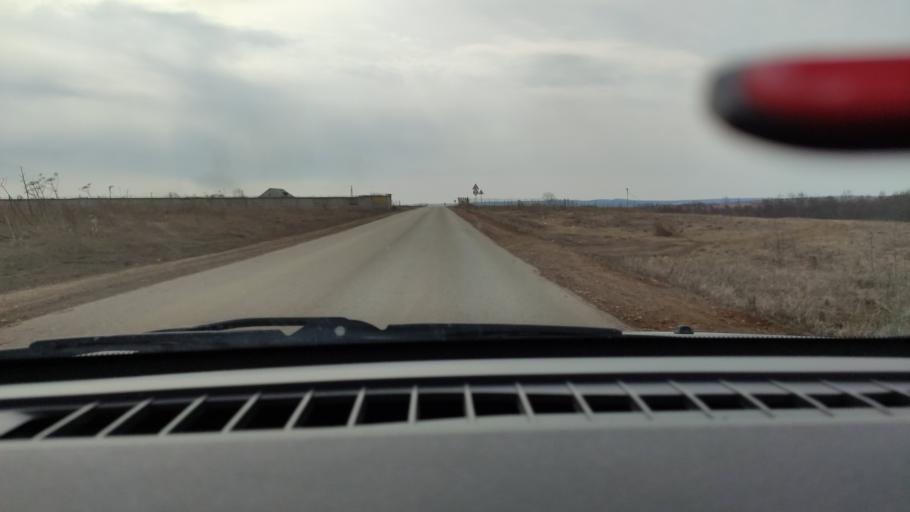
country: RU
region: Perm
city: Kultayevo
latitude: 57.9012
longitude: 55.9929
